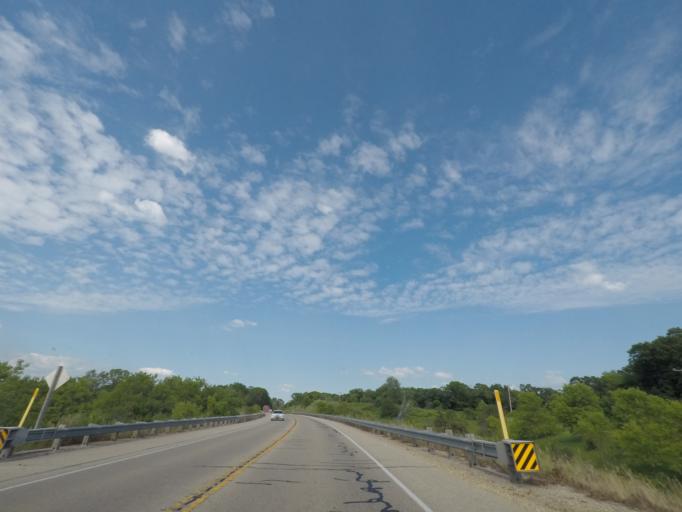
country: US
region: Wisconsin
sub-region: Jefferson County
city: Palmyra
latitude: 42.7961
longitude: -88.6146
